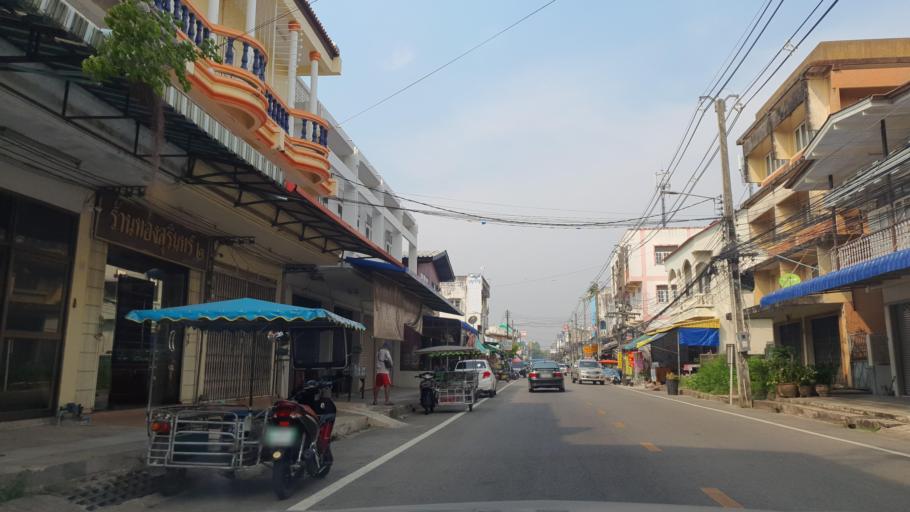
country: TH
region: Rayong
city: Rayong
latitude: 12.6224
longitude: 101.4277
